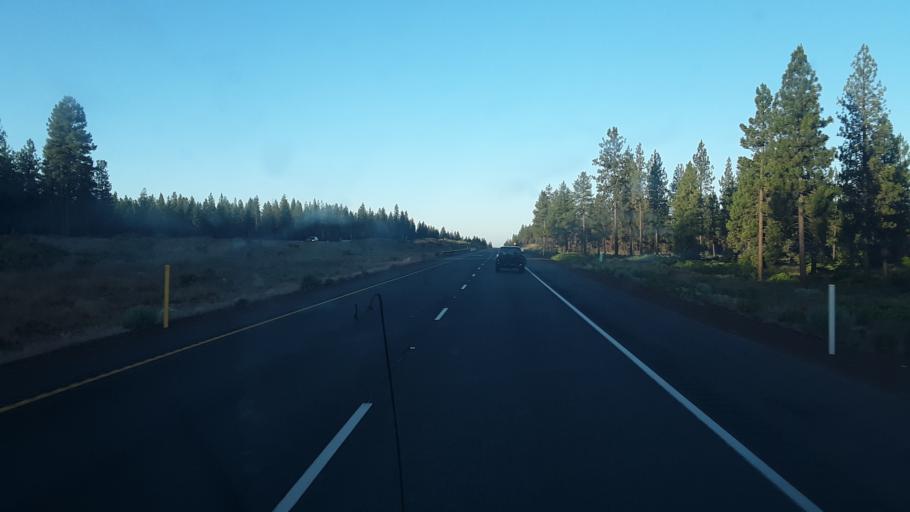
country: US
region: Oregon
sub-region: Deschutes County
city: Sunriver
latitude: 43.8716
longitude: -121.4019
